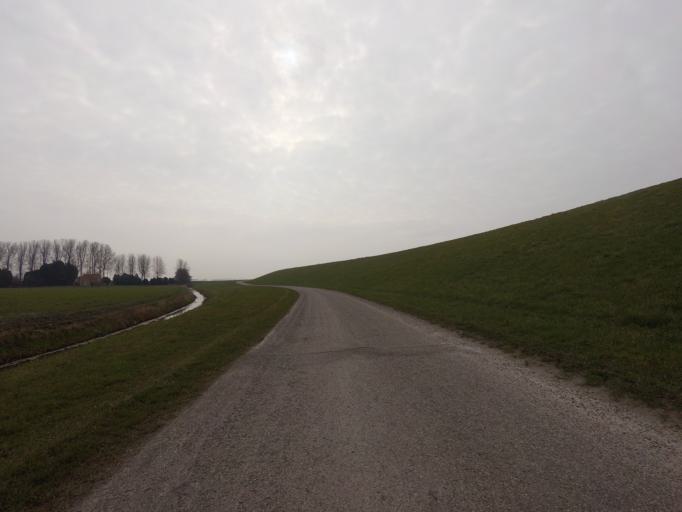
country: BE
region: Flanders
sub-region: Provincie Oost-Vlaanderen
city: Sint-Gillis-Waas
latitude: 51.3374
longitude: 4.1948
